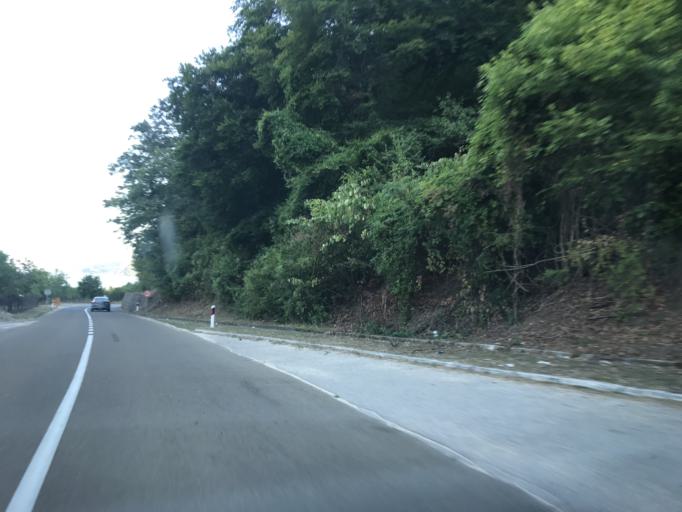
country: RO
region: Mehedinti
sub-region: Comuna Svinita
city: Svinita
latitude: 44.5100
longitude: 22.0500
